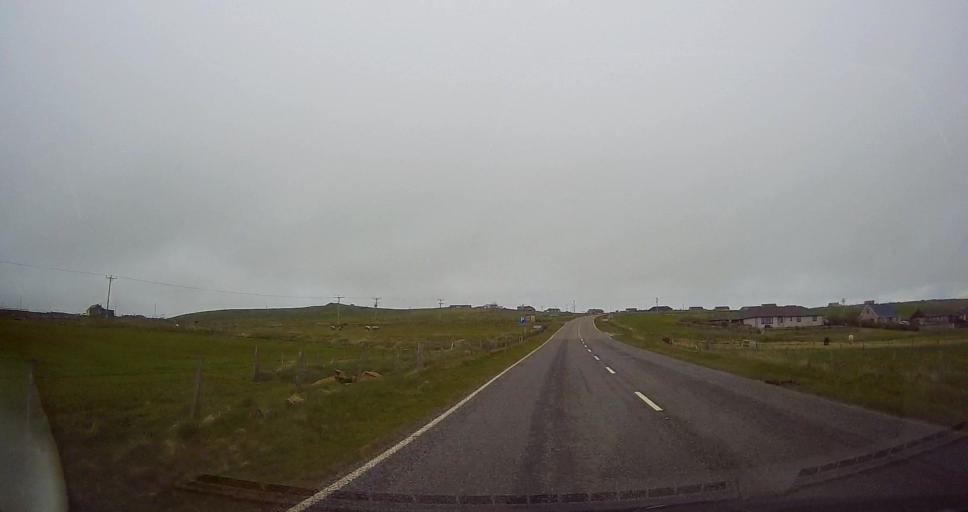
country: GB
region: Scotland
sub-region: Shetland Islands
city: Sandwick
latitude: 59.8886
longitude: -1.3032
